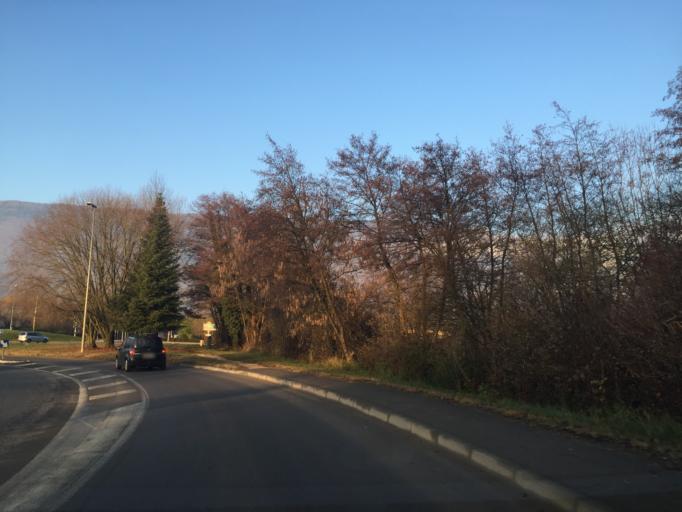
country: FR
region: Rhone-Alpes
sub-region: Departement de la Savoie
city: Viviers-du-Lac
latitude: 45.6480
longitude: 5.8947
